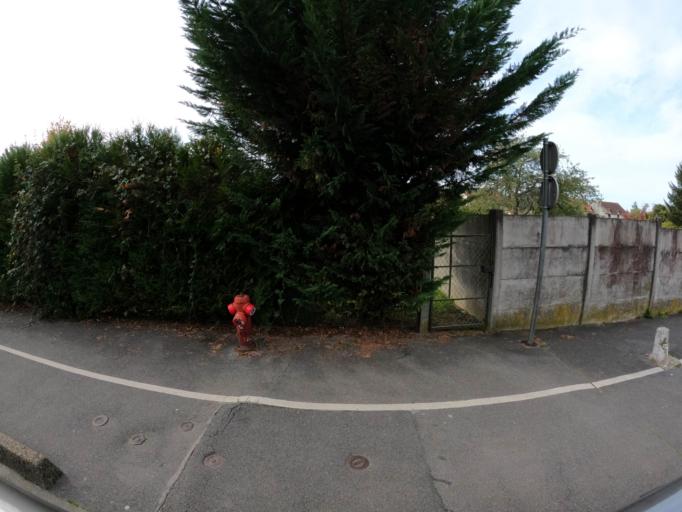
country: FR
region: Ile-de-France
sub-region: Departement de Seine-et-Marne
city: Pontault-Combault
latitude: 48.7795
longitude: 2.6042
